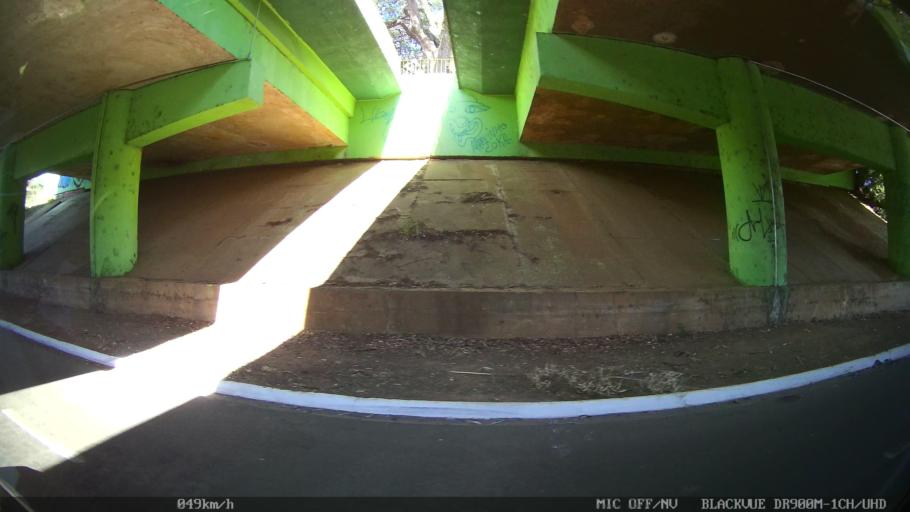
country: BR
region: Sao Paulo
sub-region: Franca
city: Franca
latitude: -20.5201
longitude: -47.3846
